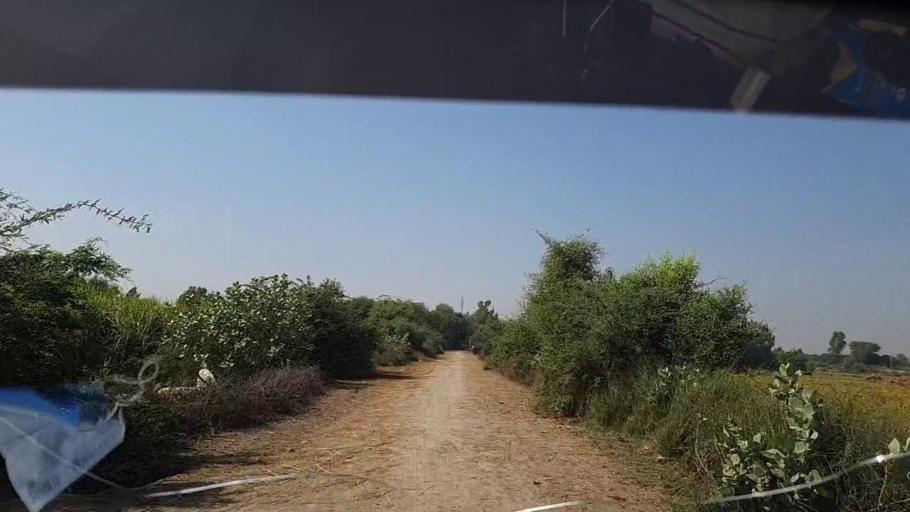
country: PK
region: Sindh
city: Naudero
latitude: 27.6941
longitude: 68.4022
